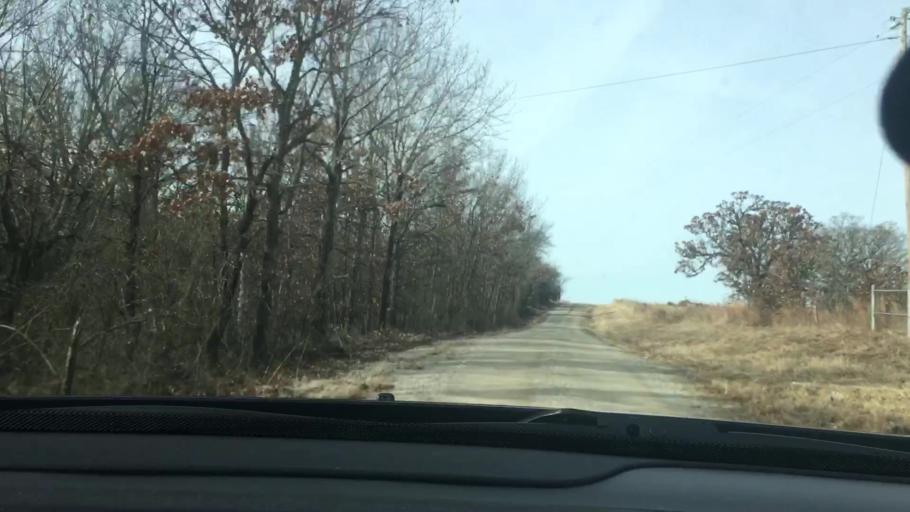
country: US
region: Oklahoma
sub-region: Garvin County
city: Wynnewood
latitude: 34.6374
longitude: -97.2301
